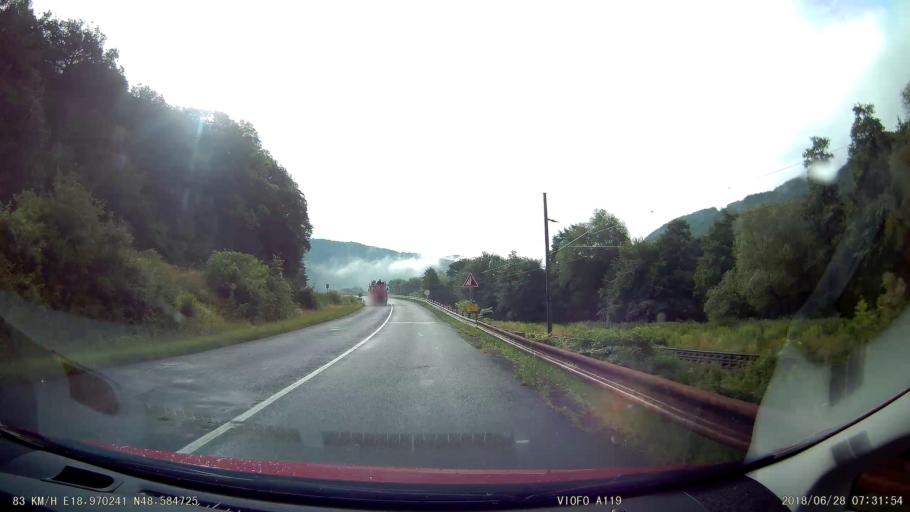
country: SK
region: Banskobystricky
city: Ziar nad Hronom
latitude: 48.5847
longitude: 18.9704
